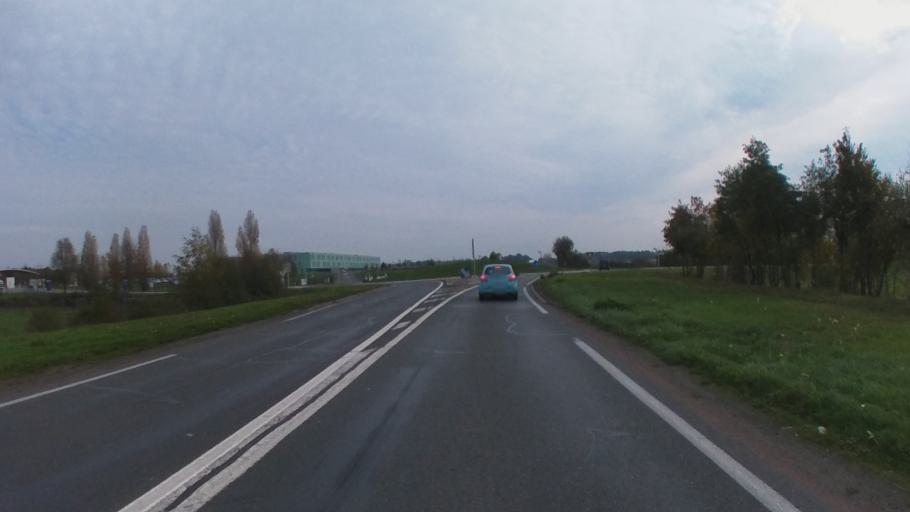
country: FR
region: Pays de la Loire
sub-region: Departement de la Sarthe
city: Vion
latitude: 47.7744
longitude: -0.2118
